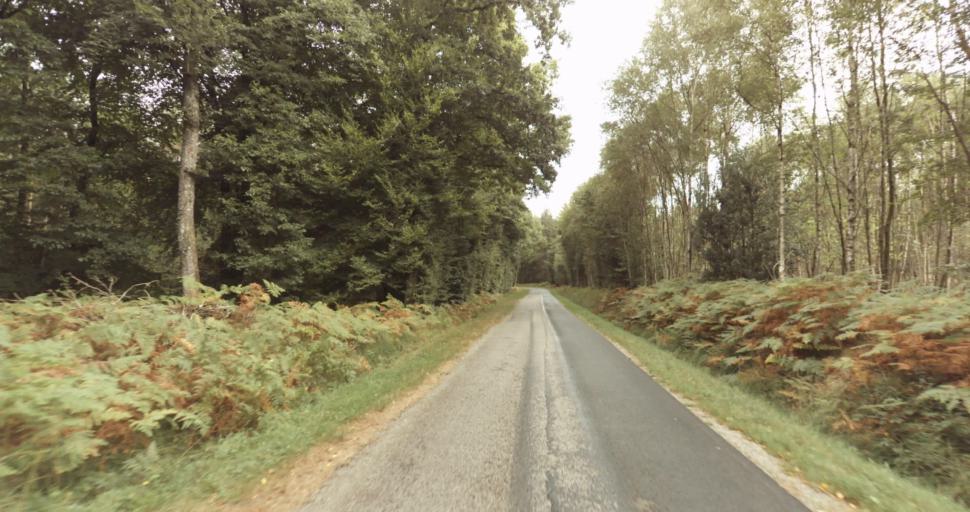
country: FR
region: Lower Normandy
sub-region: Departement de l'Orne
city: Gace
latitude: 48.8283
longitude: 0.3376
